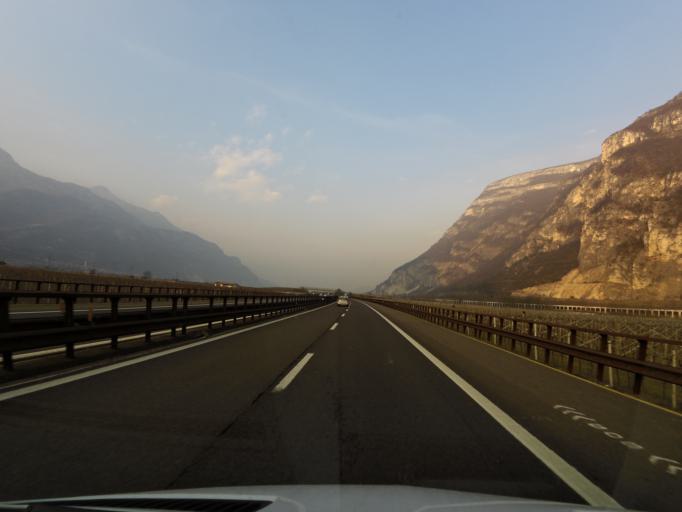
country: IT
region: Trentino-Alto Adige
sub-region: Provincia di Trento
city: Besenello
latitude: 45.9559
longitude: 11.1049
